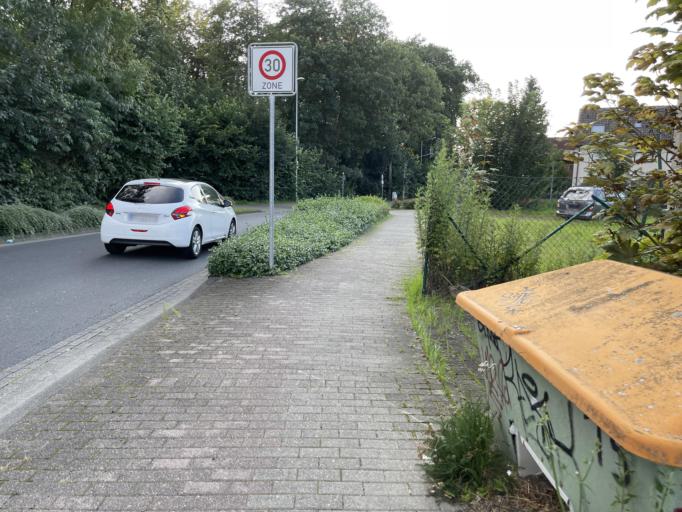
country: DE
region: North Rhine-Westphalia
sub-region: Regierungsbezirk Koln
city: Bergheim
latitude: 50.9447
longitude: 6.6471
